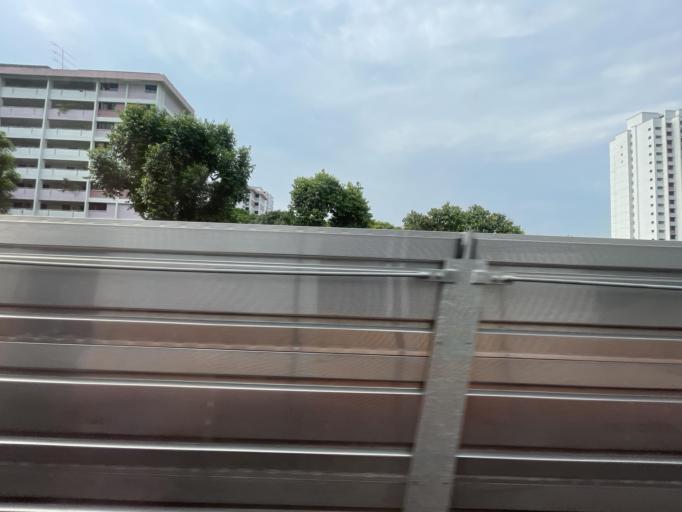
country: SG
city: Singapore
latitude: 1.3122
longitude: 103.7705
